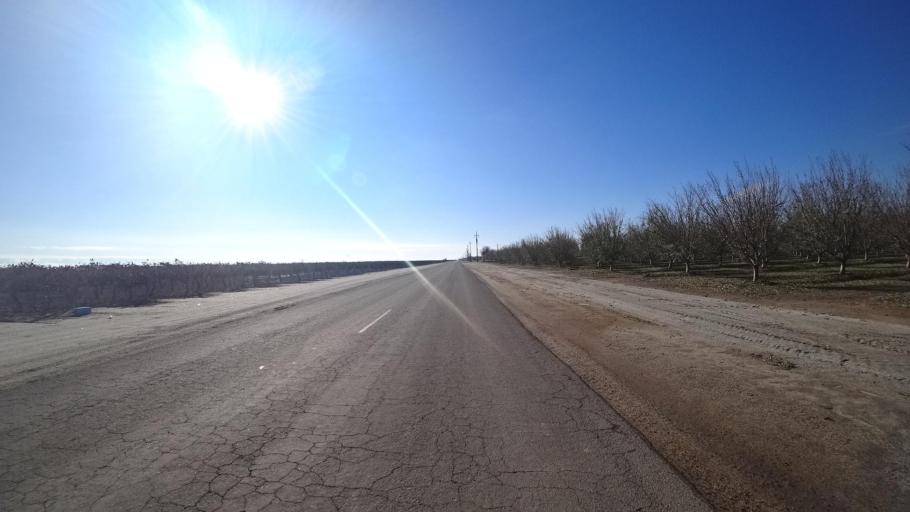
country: US
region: California
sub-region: Kern County
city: Delano
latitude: 35.7284
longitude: -119.2763
